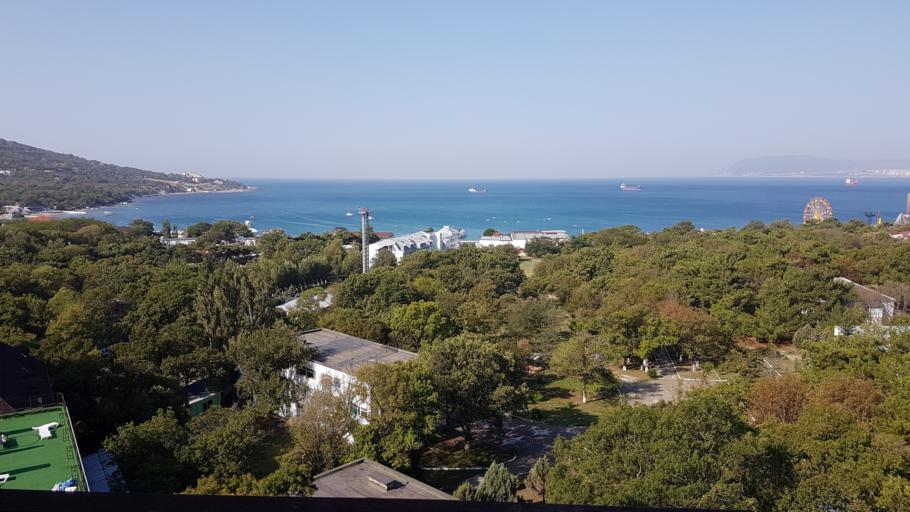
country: RU
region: Krasnodarskiy
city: Kabardinka
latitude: 44.6506
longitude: 37.9369
